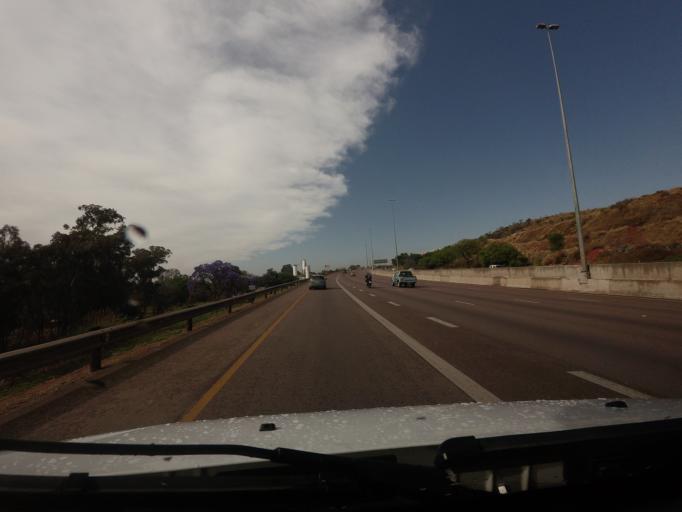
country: ZA
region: Gauteng
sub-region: City of Tshwane Metropolitan Municipality
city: Pretoria
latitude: -25.6920
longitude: 28.2830
